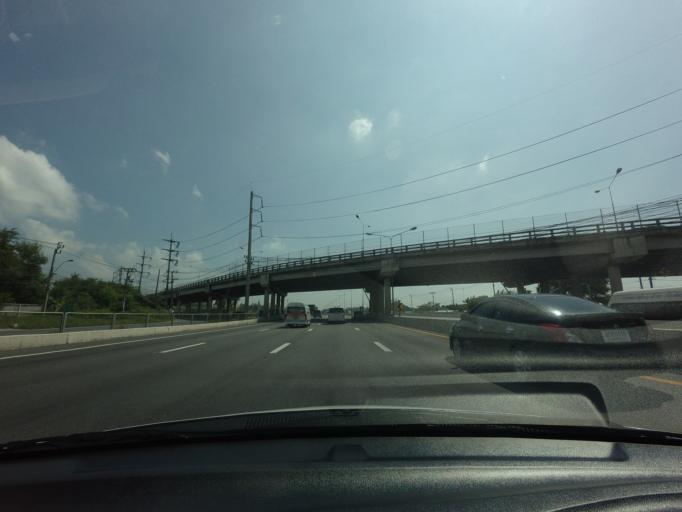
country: TH
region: Bangkok
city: Lat Krabang
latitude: 13.7324
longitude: 100.7840
